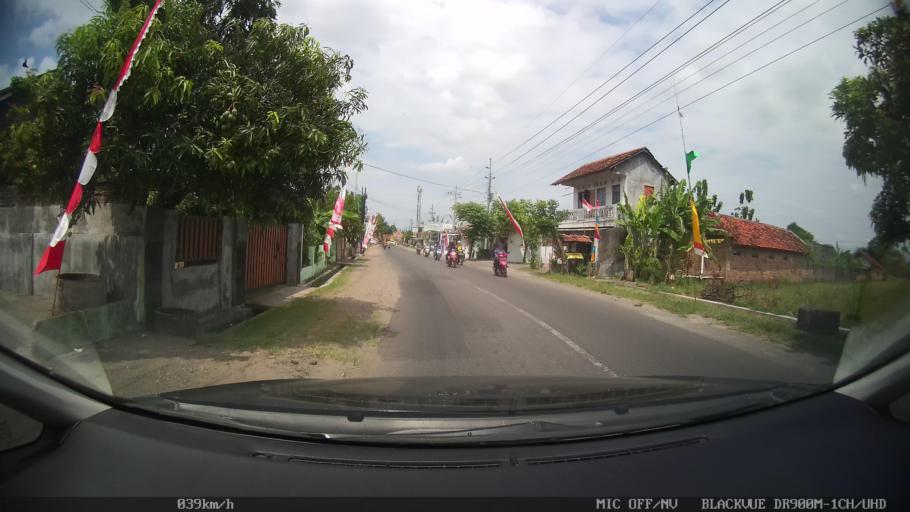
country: ID
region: Daerah Istimewa Yogyakarta
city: Depok
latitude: -7.8035
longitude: 110.4528
